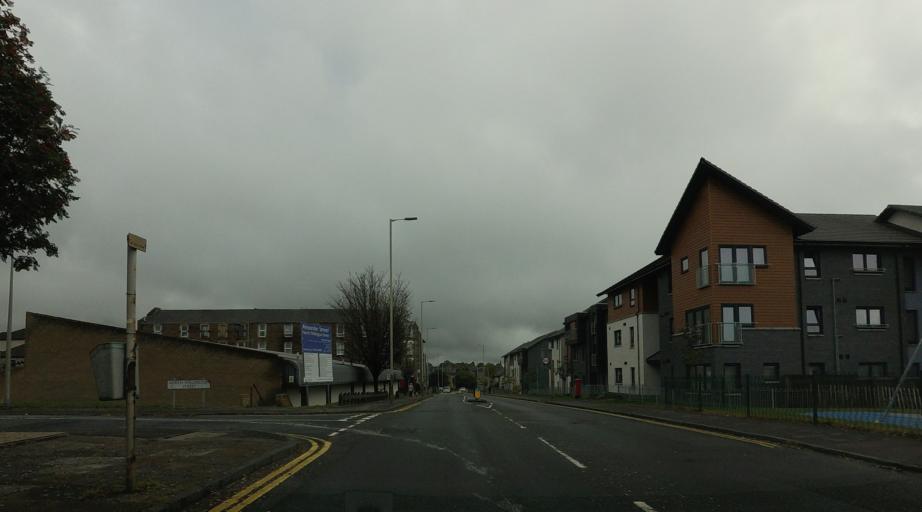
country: GB
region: Scotland
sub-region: Dundee City
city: Dundee
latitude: 56.4694
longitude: -2.9696
